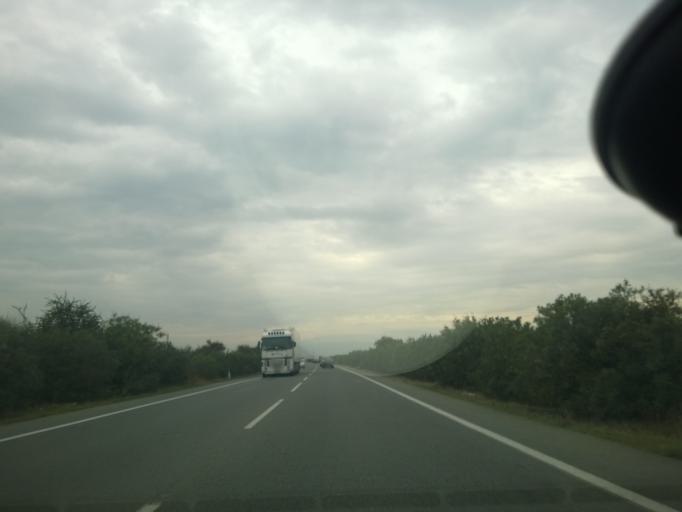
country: GR
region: Central Macedonia
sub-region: Nomos Pellis
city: Palaifyto
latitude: 40.8084
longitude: 22.2372
